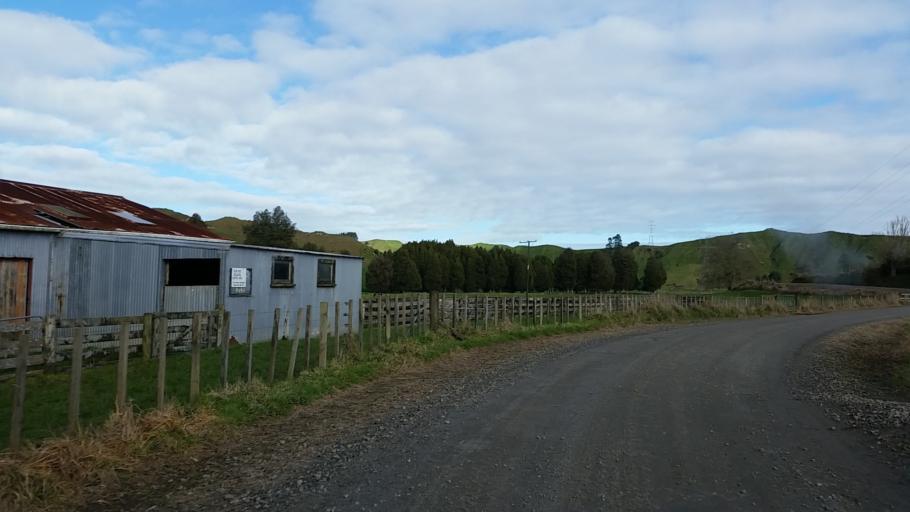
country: NZ
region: Taranaki
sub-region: South Taranaki District
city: Eltham
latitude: -39.2567
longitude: 174.5182
